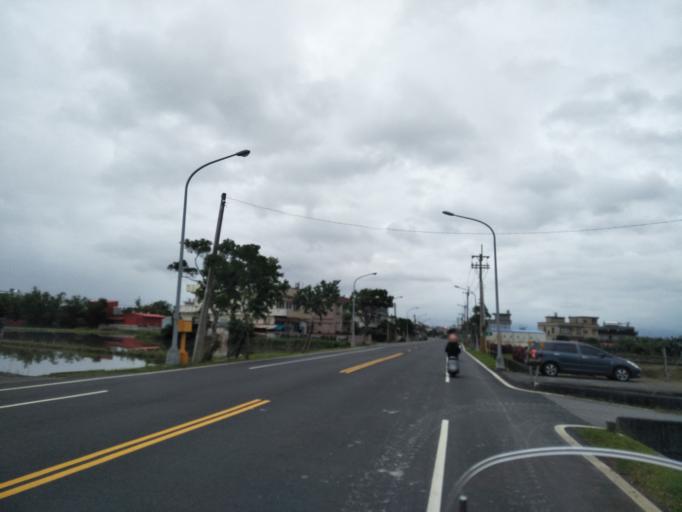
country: TW
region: Taiwan
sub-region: Yilan
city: Yilan
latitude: 24.7780
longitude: 121.7831
